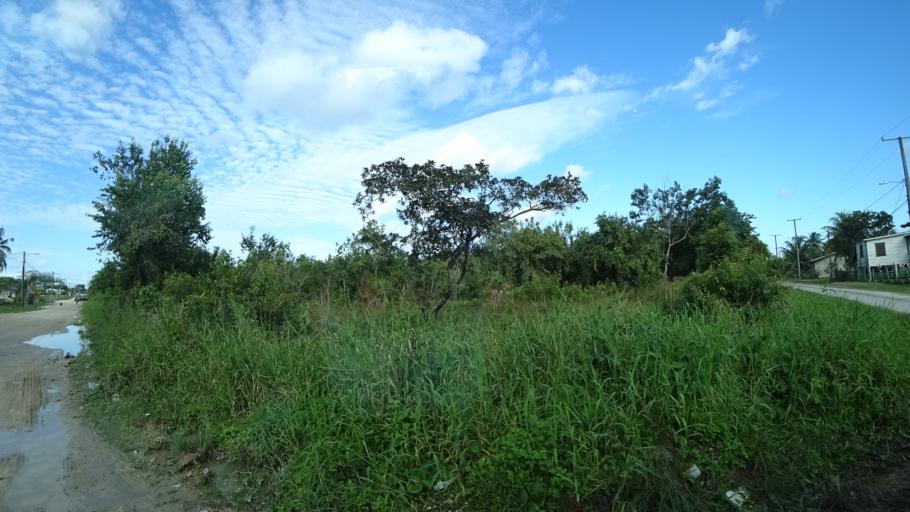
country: BZ
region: Belize
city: Belize City
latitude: 17.5656
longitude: -88.4086
